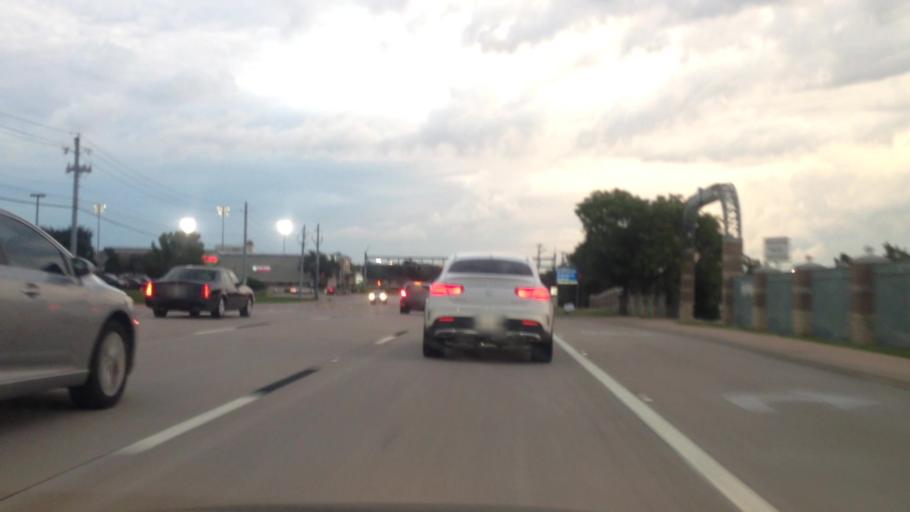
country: US
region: Texas
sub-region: Tarrant County
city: Hurst
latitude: 32.8536
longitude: -97.1860
